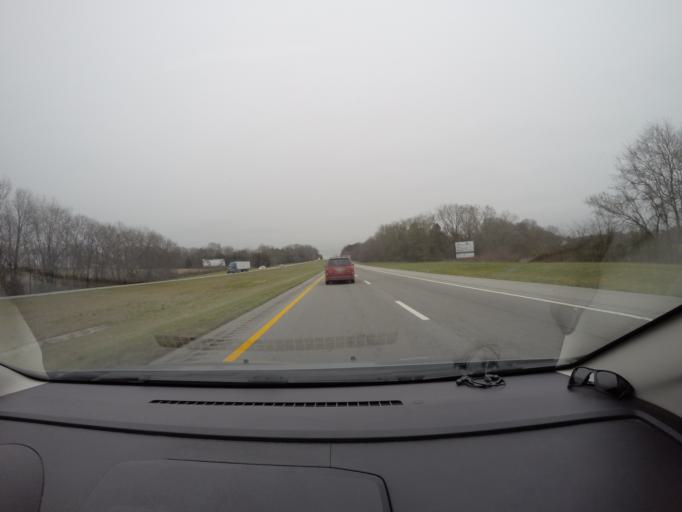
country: US
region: Tennessee
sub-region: Coffee County
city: Manchester
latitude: 35.3710
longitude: -85.9697
